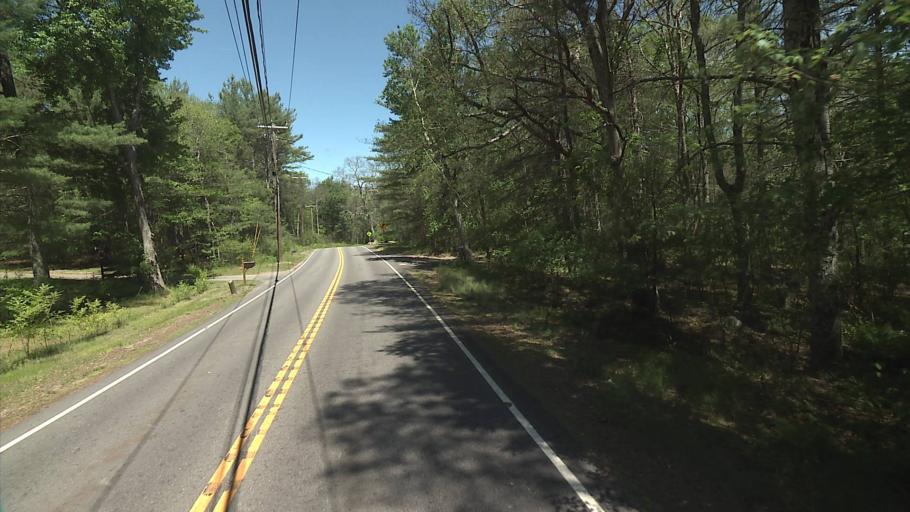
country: US
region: Connecticut
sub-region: New London County
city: Preston City
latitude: 41.5666
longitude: -71.8568
